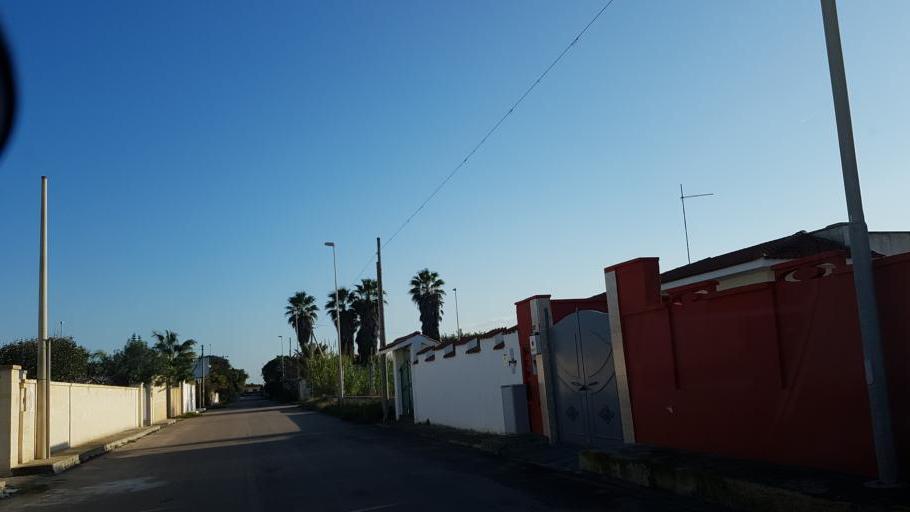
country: IT
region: Apulia
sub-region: Provincia di Brindisi
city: Torchiarolo
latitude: 40.5141
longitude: 18.0973
